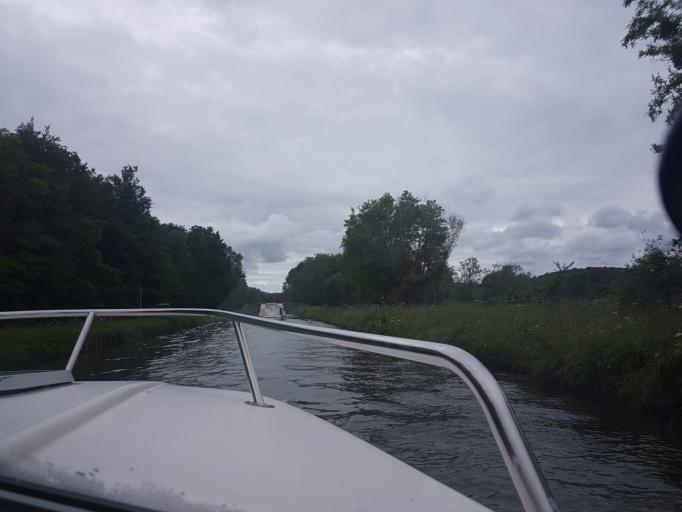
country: FR
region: Bourgogne
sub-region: Departement de l'Yonne
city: Vermenton
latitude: 47.6524
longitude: 3.6700
